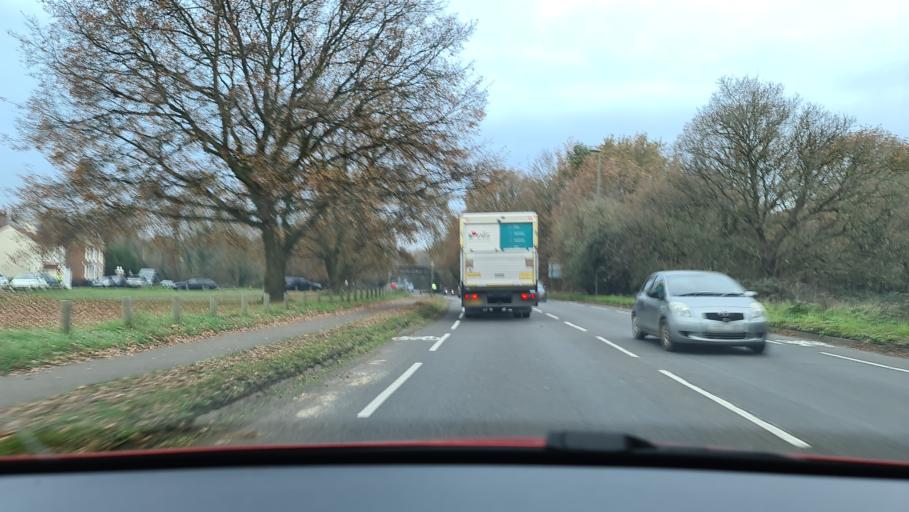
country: GB
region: England
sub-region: Surrey
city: Thames Ditton
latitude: 51.3820
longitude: -0.3478
